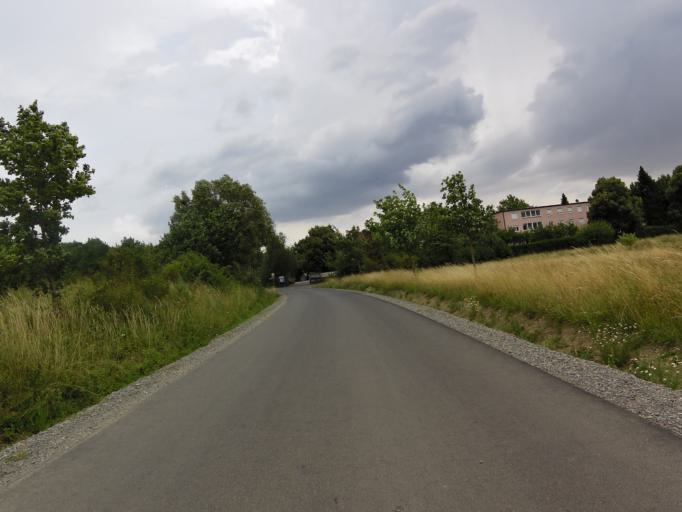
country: DE
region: Bavaria
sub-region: Regierungsbezirk Unterfranken
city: Randersacker
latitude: 49.7739
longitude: 9.9730
